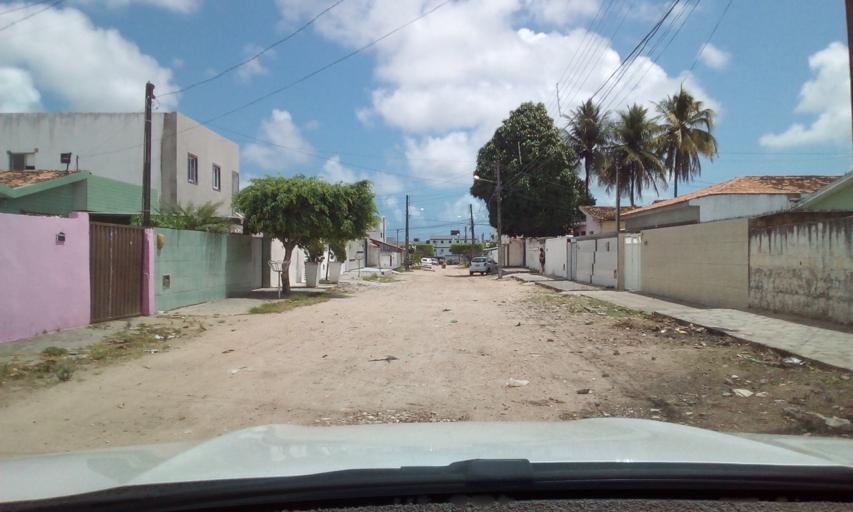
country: BR
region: Paraiba
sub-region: Joao Pessoa
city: Joao Pessoa
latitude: -7.1783
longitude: -34.8665
